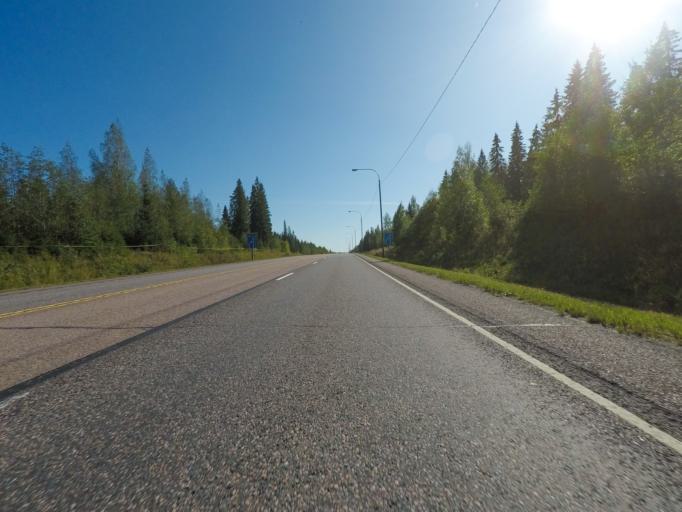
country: FI
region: Northern Savo
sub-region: Varkaus
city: Varkaus
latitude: 62.3727
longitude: 27.8095
